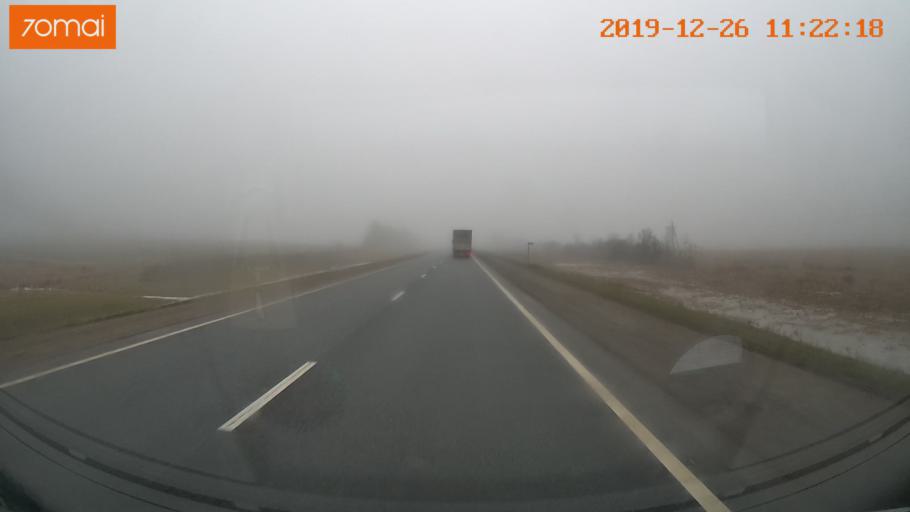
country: RU
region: Vologda
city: Chebsara
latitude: 59.1275
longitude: 38.9474
